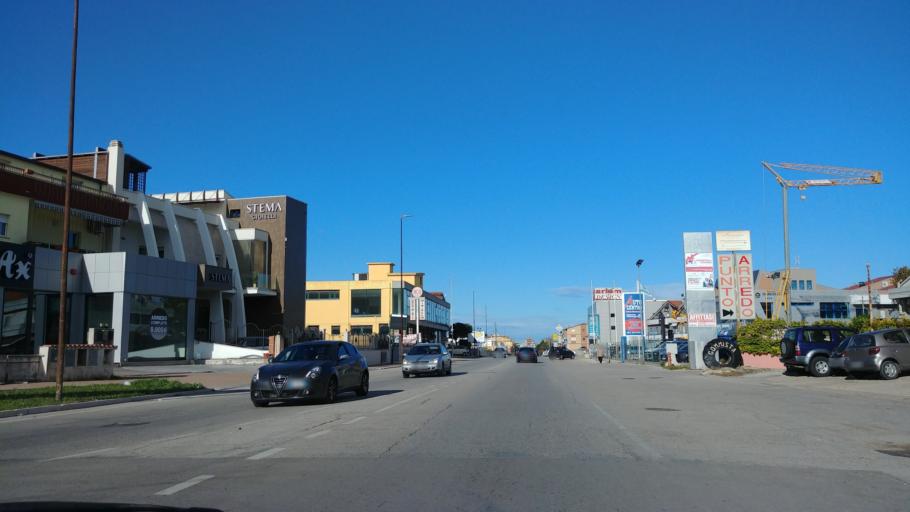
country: IT
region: Molise
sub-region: Provincia di Campobasso
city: Termoli
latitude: 41.9866
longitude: 15.0031
